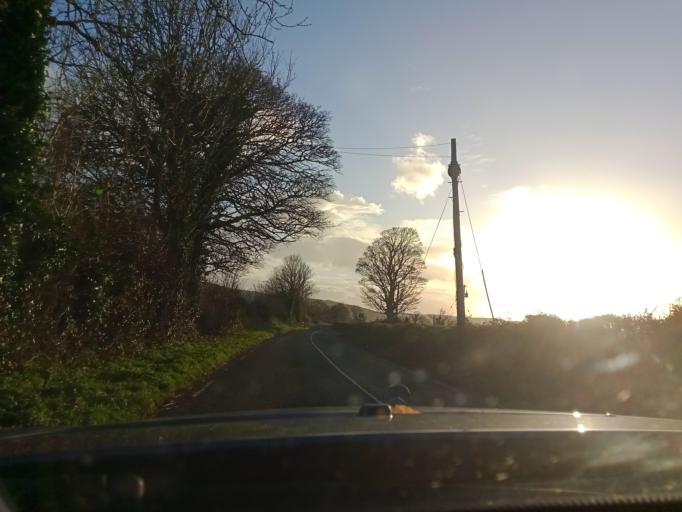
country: IE
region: Leinster
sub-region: Kilkenny
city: Callan
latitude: 52.4827
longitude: -7.3258
